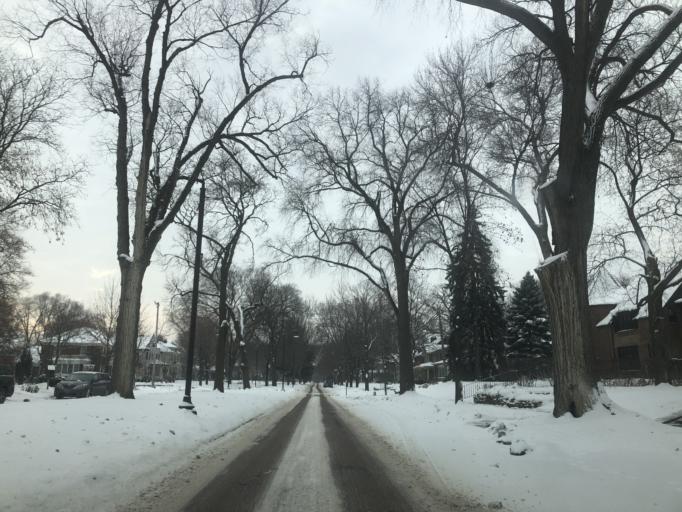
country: US
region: Minnesota
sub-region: Hennepin County
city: Richfield
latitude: 44.9239
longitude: -93.2936
